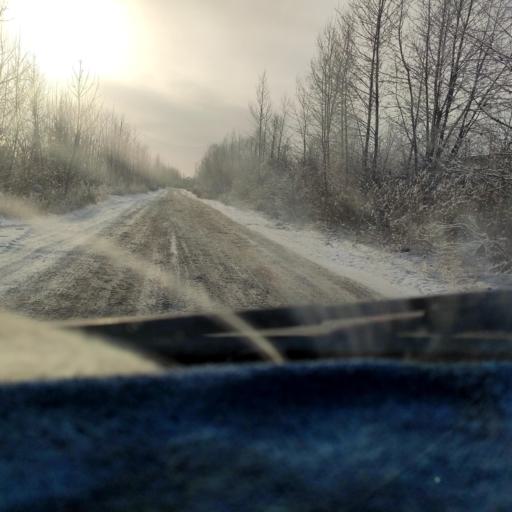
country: RU
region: Bashkortostan
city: Avdon
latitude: 54.6728
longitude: 55.8161
